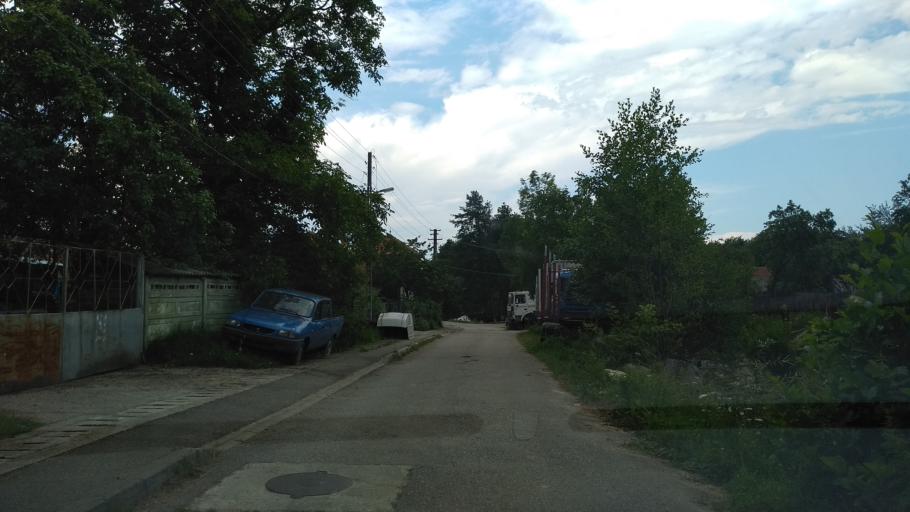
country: RO
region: Hunedoara
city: Salasu de Sus
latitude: 45.4884
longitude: 22.9447
